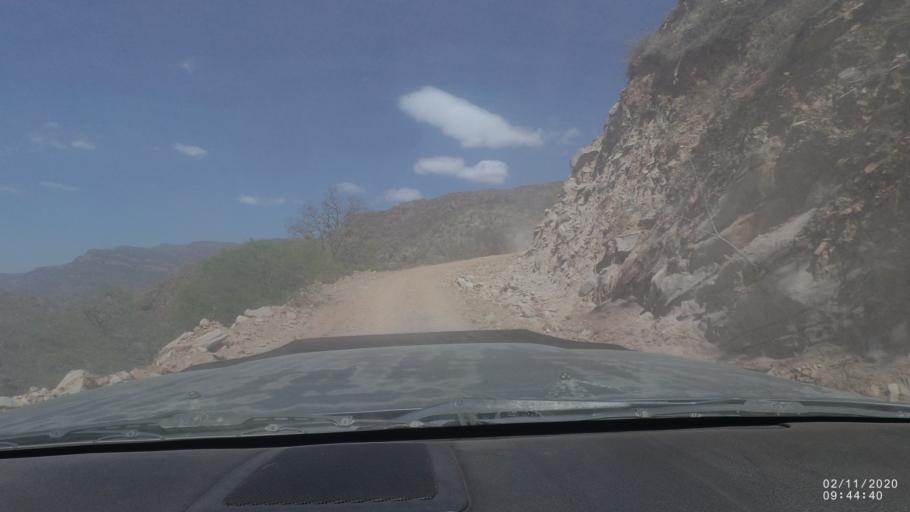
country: BO
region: Chuquisaca
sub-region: Provincia Zudanez
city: Mojocoya
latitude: -18.3898
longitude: -64.6108
